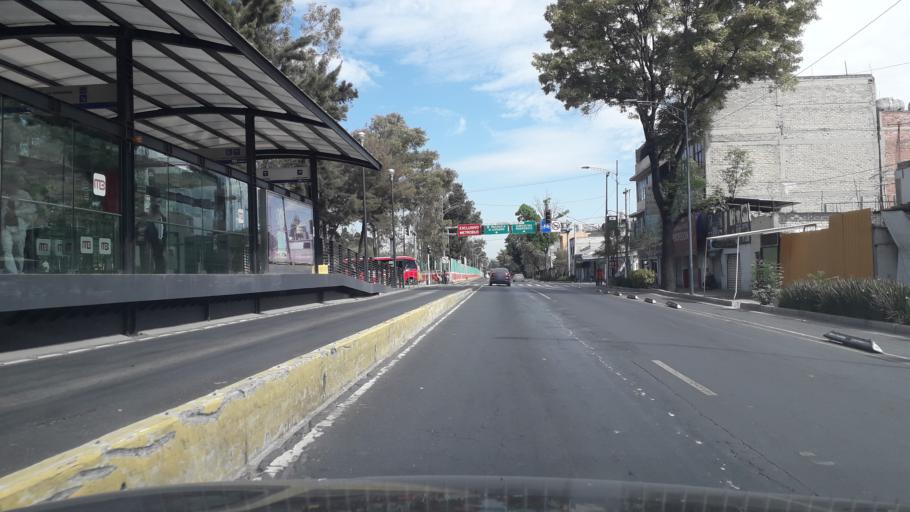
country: MX
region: Mexico City
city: Gustavo A. Madero
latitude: 19.4969
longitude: -99.0899
